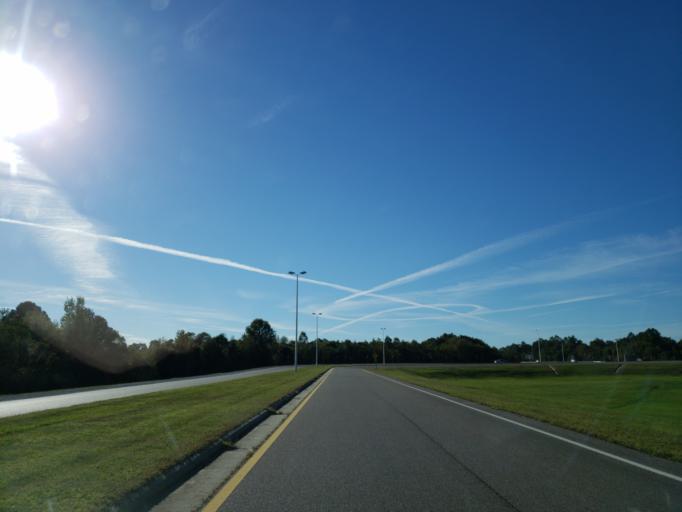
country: US
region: Mississippi
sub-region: Forrest County
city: Petal
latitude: 31.3580
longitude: -89.2727
